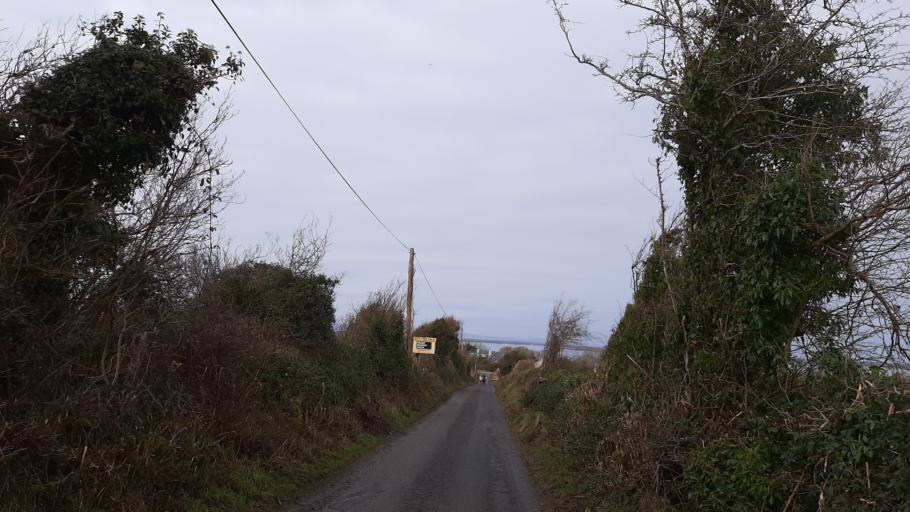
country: IE
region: Connaught
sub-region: County Galway
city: Gaillimh
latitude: 53.3164
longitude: -9.0547
